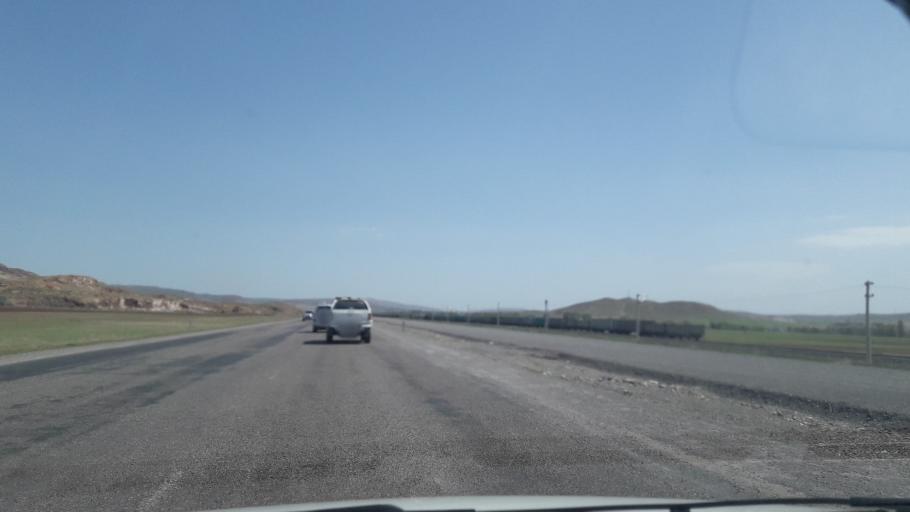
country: TR
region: Sivas
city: Ulas
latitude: 39.5332
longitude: 37.0169
